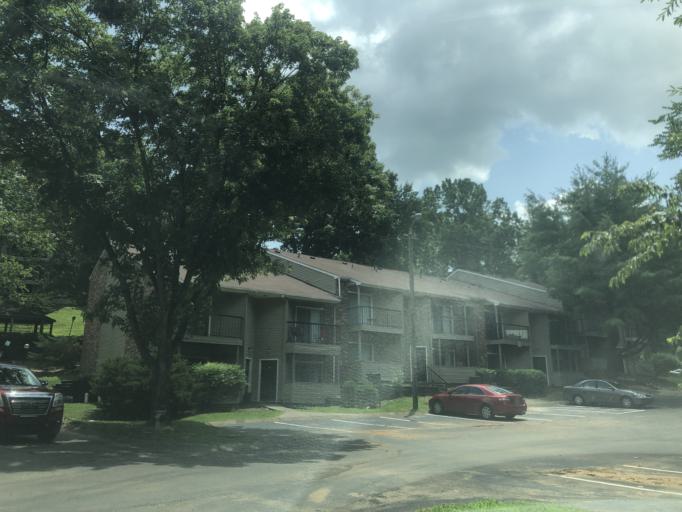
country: US
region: Tennessee
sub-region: Williamson County
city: Brentwood Estates
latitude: 36.0483
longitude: -86.6853
